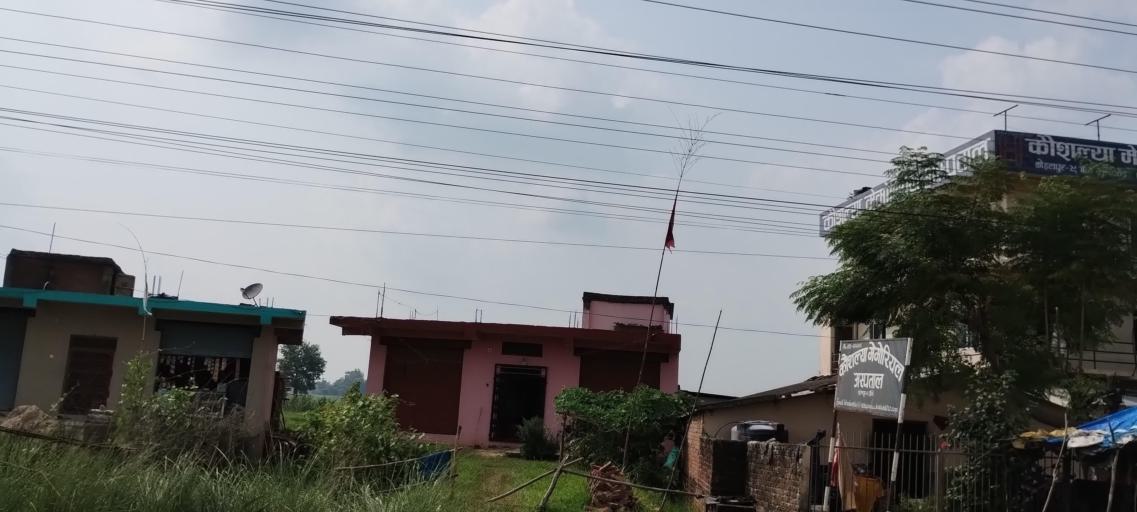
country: NP
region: Mid Western
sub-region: Bheri Zone
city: Nepalgunj
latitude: 28.1582
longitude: 81.6702
